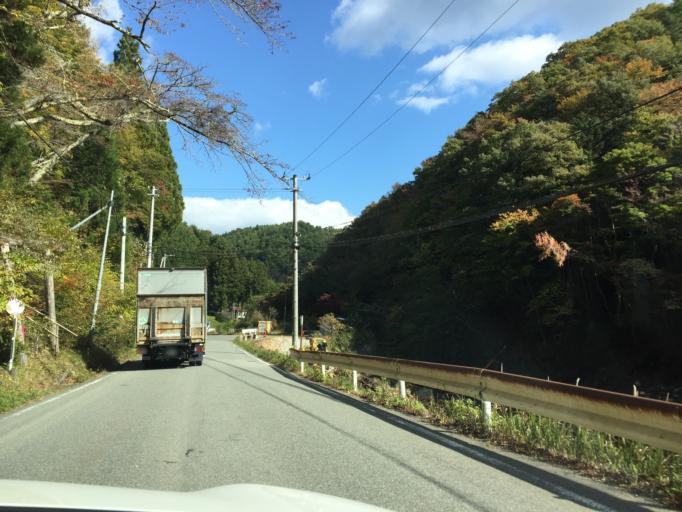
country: JP
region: Fukushima
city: Namie
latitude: 37.3516
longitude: 140.8929
